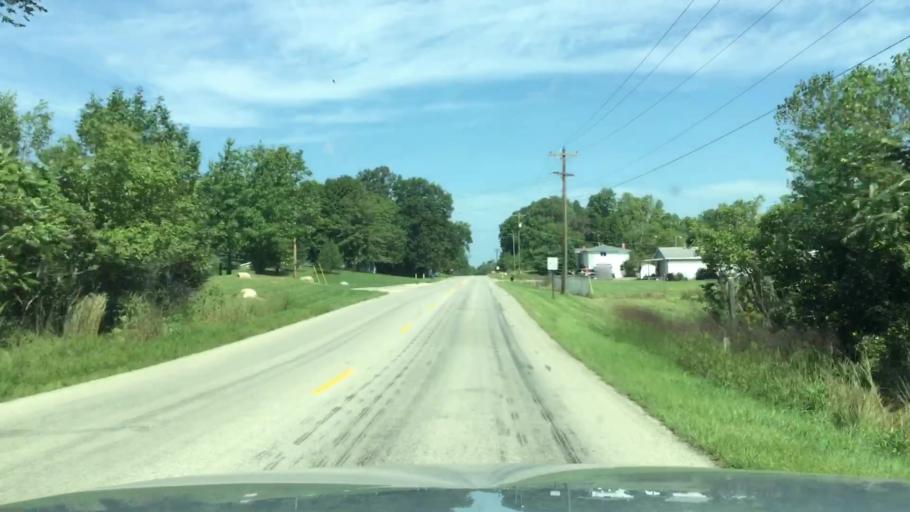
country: US
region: Michigan
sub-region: Lenawee County
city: Manitou Beach-Devils Lake
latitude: 42.0283
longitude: -84.2763
